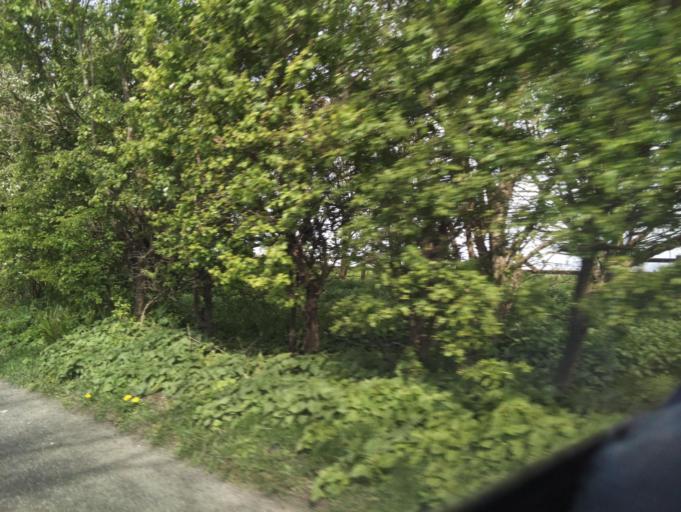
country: GB
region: England
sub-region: Somerset
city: Street
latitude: 51.1102
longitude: -2.7550
